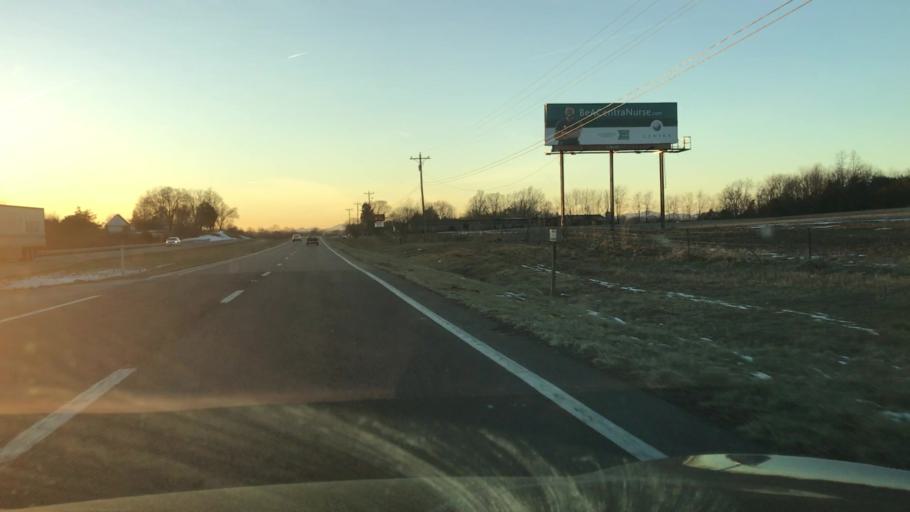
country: US
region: Virginia
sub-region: Bedford County
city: Forest
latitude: 37.3007
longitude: -79.3666
